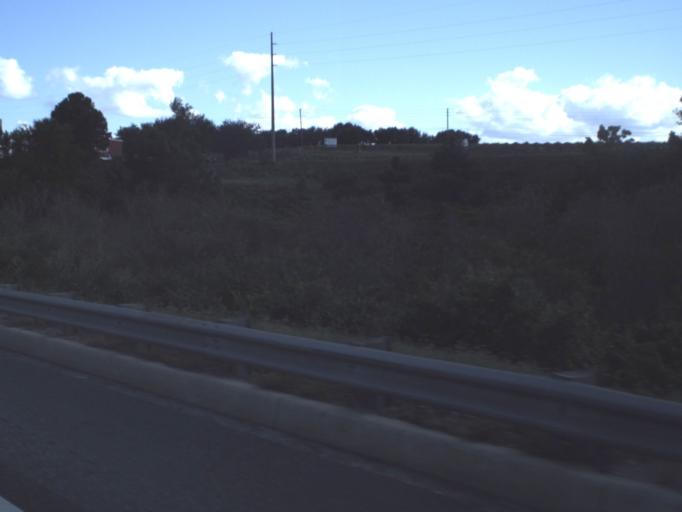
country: US
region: Florida
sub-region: Lake County
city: Minneola
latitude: 28.6317
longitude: -81.7711
